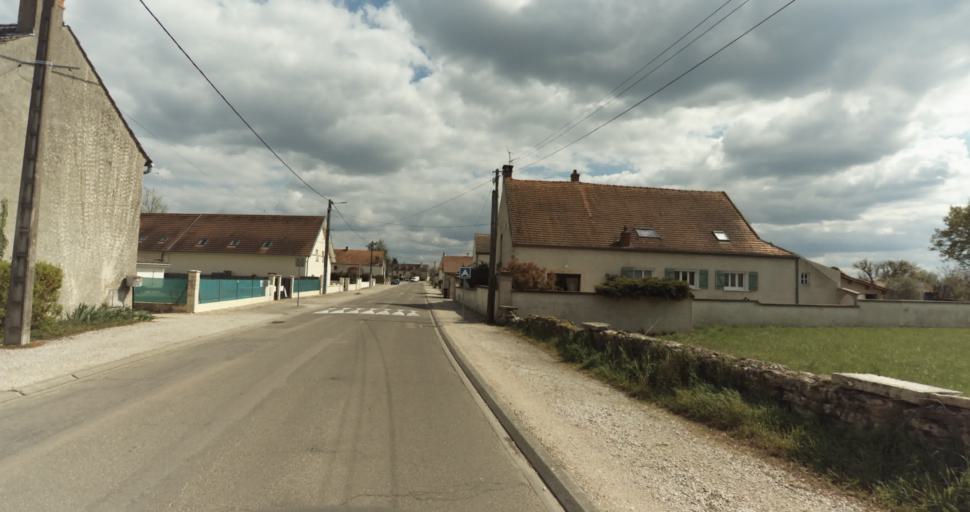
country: FR
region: Bourgogne
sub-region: Departement de la Cote-d'Or
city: Auxonne
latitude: 47.1853
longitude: 5.3936
